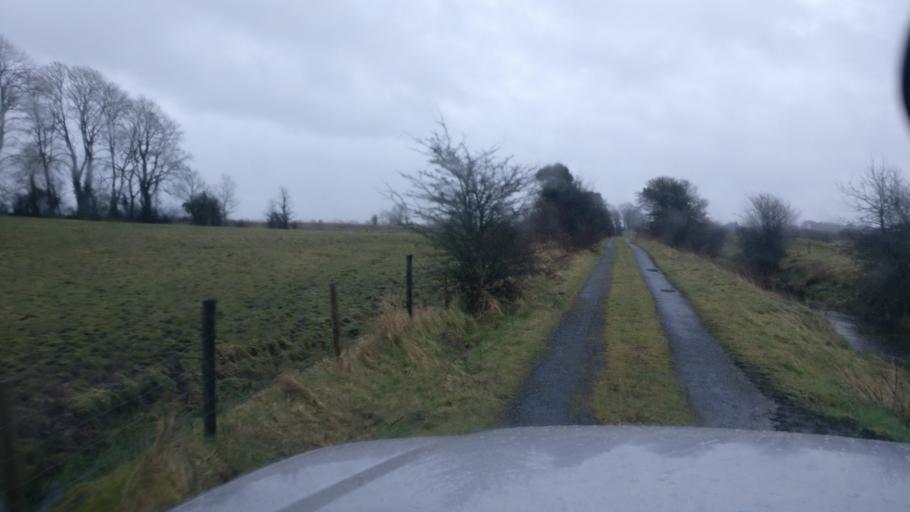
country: IE
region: Connaught
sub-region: County Galway
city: Ballinasloe
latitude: 53.2438
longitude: -8.3388
